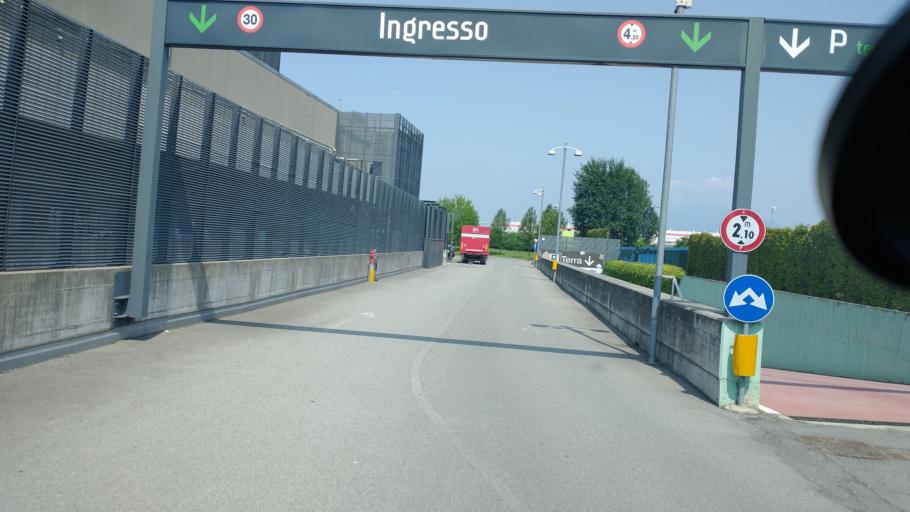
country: IT
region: Lombardy
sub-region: Provincia di Bergamo
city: Lallio
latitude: 45.6484
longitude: 9.6315
